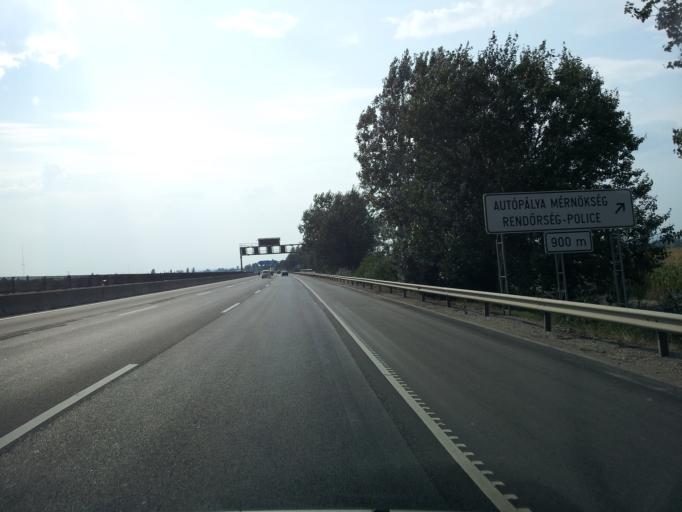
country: HU
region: Pest
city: Dunaharaszti
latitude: 47.3774
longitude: 19.0733
